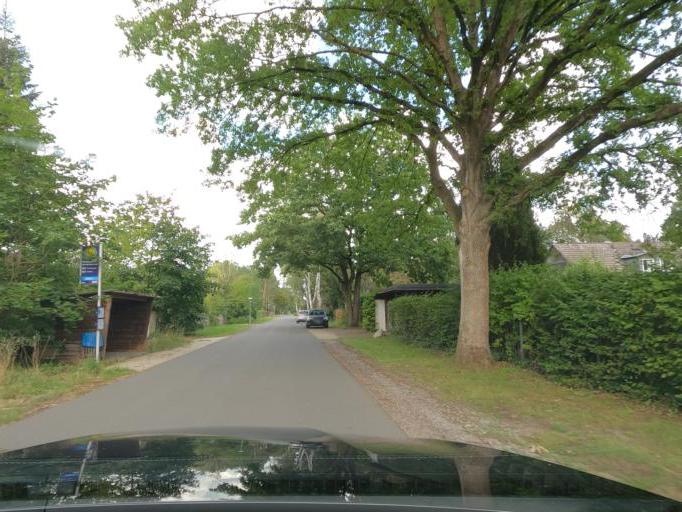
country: DE
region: Lower Saxony
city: Isernhagen Farster Bauerschaft
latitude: 52.5241
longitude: 9.8708
